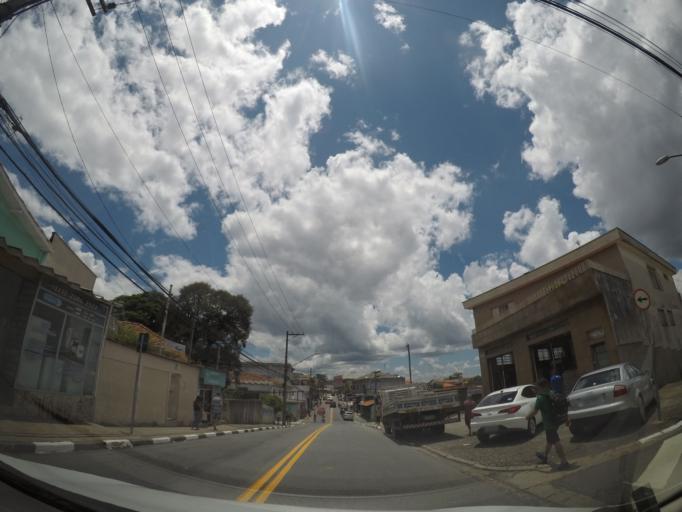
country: BR
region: Sao Paulo
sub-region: Guarulhos
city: Guarulhos
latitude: -23.4584
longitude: -46.5457
